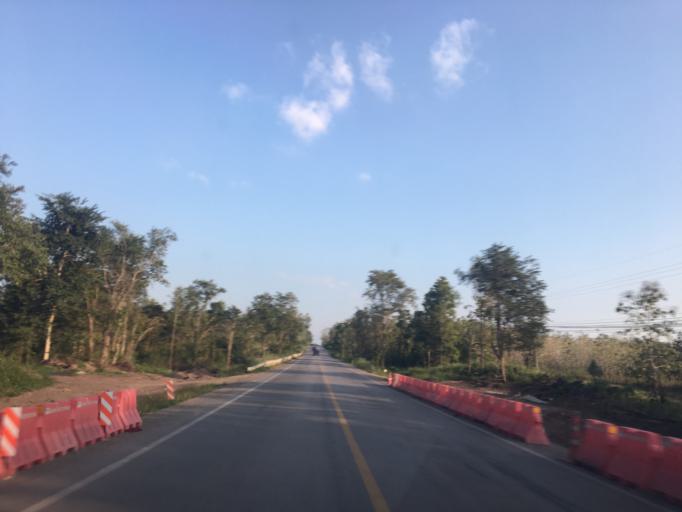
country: TH
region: Lampang
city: Ngao
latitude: 18.7055
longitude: 99.9938
